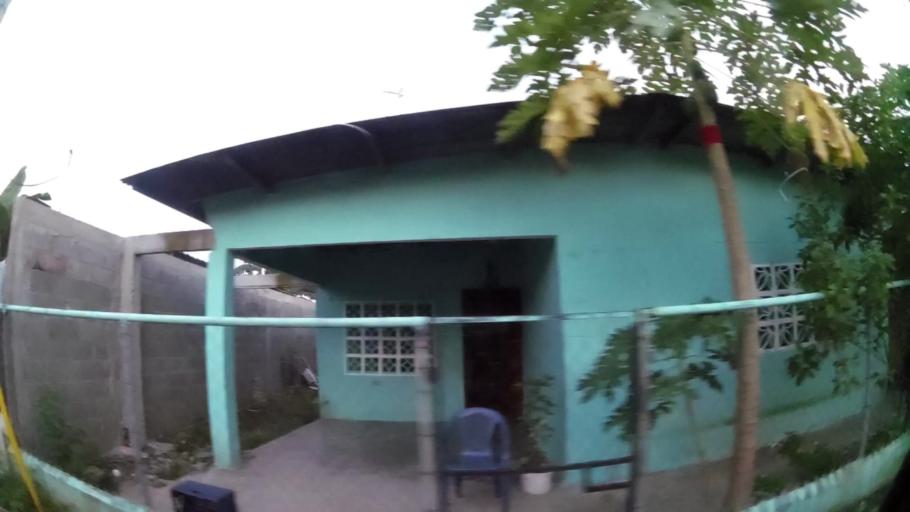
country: PA
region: Panama
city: Tocumen
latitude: 9.0792
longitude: -79.3954
